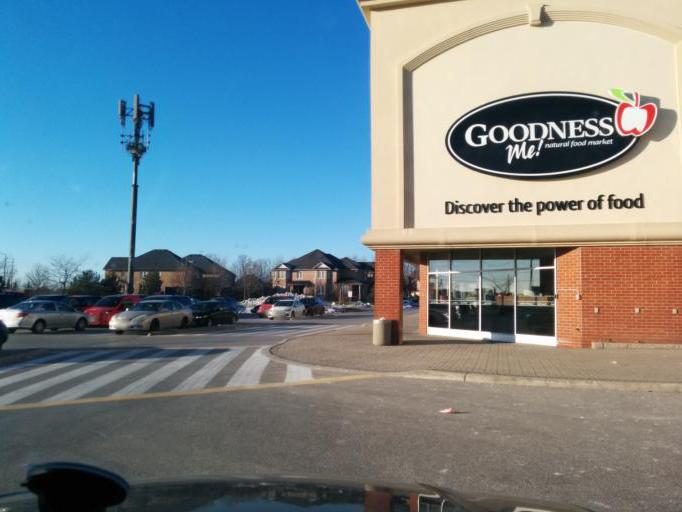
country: CA
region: Ontario
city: Mississauga
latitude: 43.5988
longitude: -79.6793
